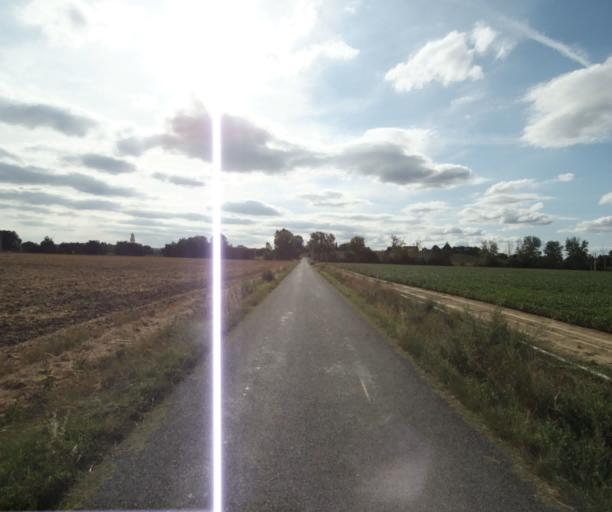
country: FR
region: Midi-Pyrenees
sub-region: Departement du Tarn
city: Puylaurens
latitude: 43.5196
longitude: 1.9961
